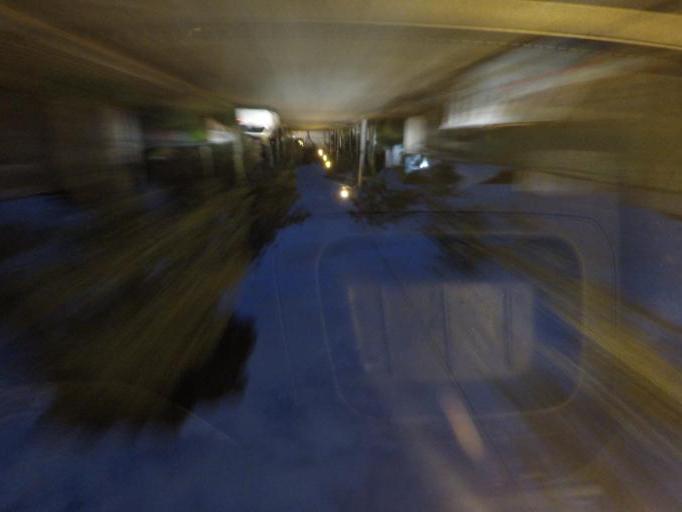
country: BR
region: Parana
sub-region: Curitiba
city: Curitiba
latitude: -25.4206
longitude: -49.2315
